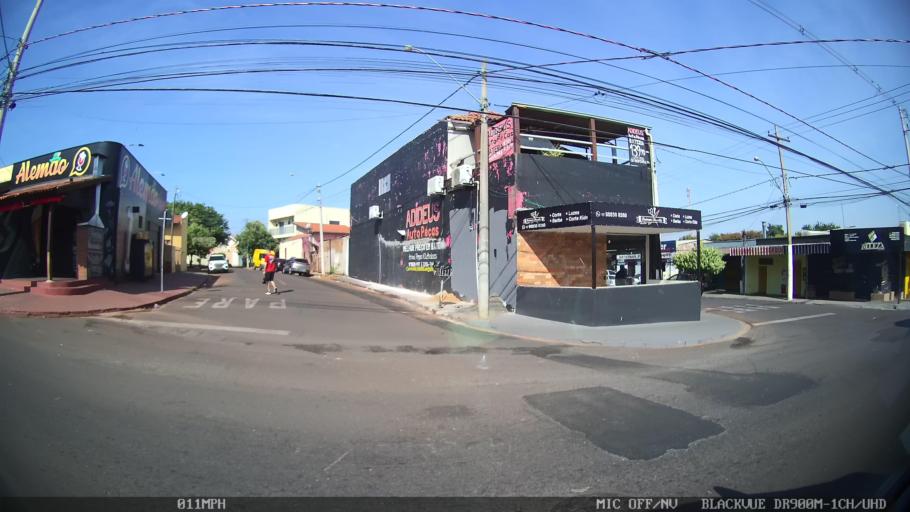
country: BR
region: Sao Paulo
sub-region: Sao Jose Do Rio Preto
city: Sao Jose do Rio Preto
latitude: -20.7918
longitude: -49.4047
